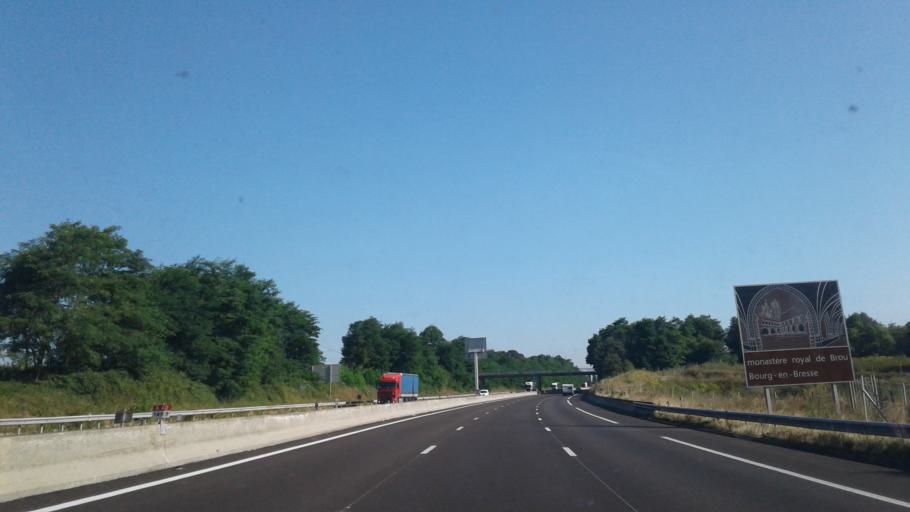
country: FR
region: Rhone-Alpes
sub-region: Departement de l'Ain
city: Saint-Martin-du-Mont
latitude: 46.0892
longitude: 5.2885
